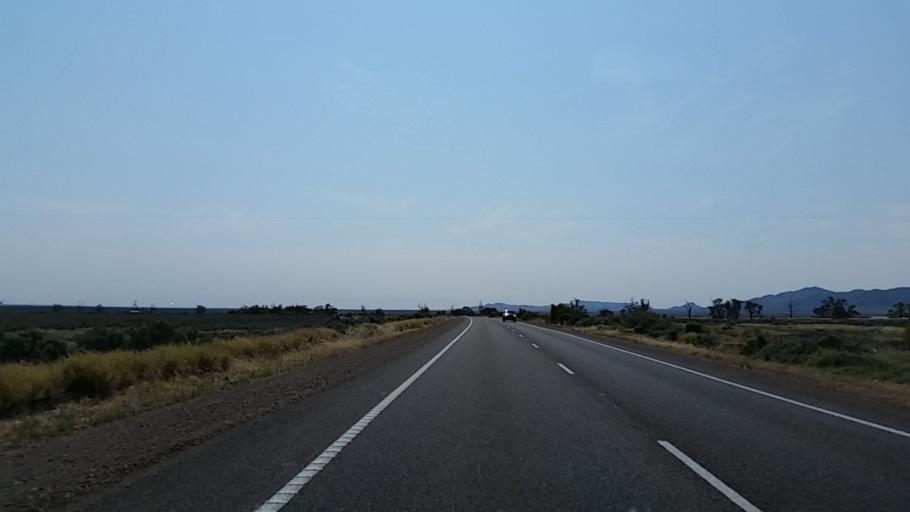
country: AU
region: South Australia
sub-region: Port Augusta
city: Port Augusta
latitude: -32.6959
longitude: 137.9420
